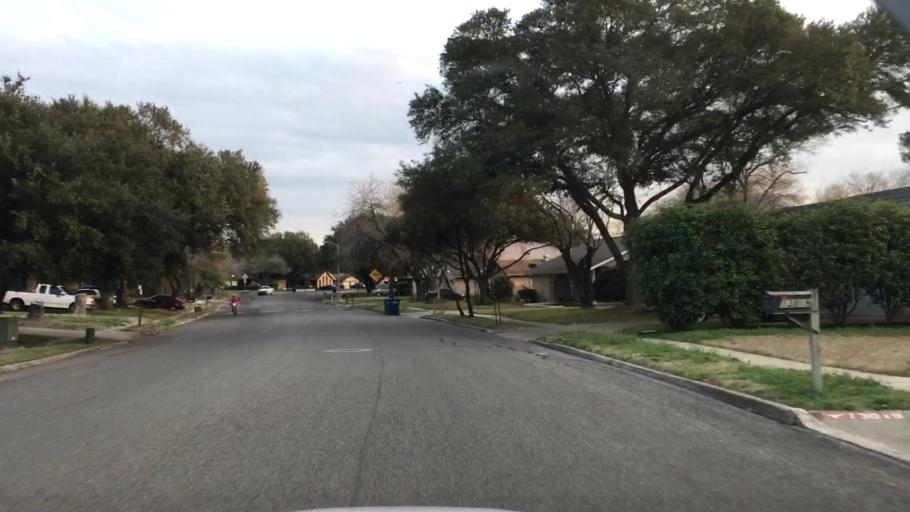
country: US
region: Texas
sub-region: Bexar County
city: Windcrest
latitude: 29.5577
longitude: -98.3930
